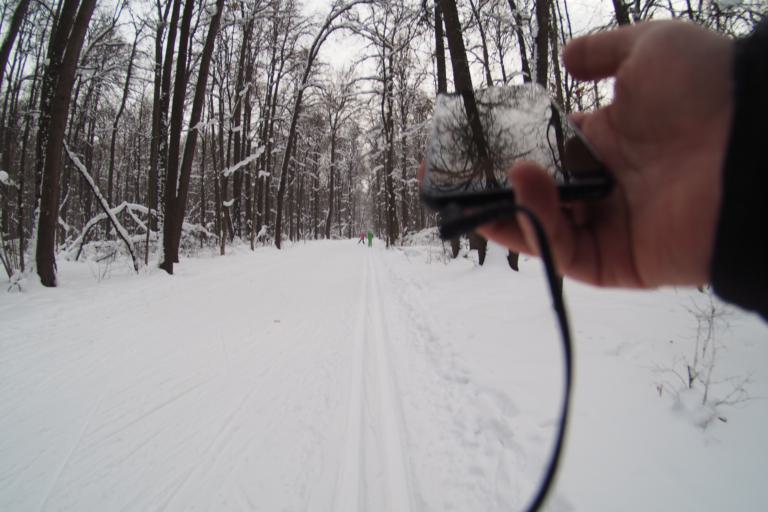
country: RU
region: Moskovskaya
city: Izmaylovo
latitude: 55.7697
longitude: 37.7774
